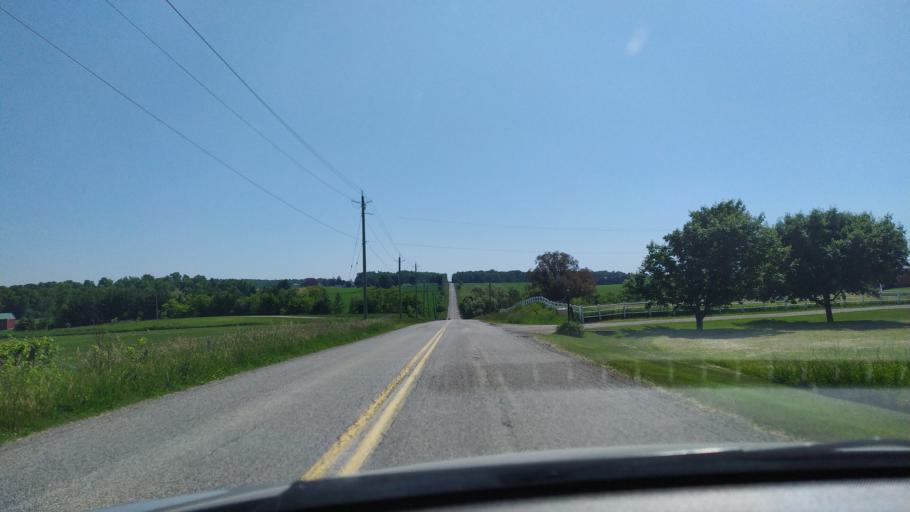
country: CA
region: Ontario
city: Stratford
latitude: 43.4554
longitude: -80.7423
